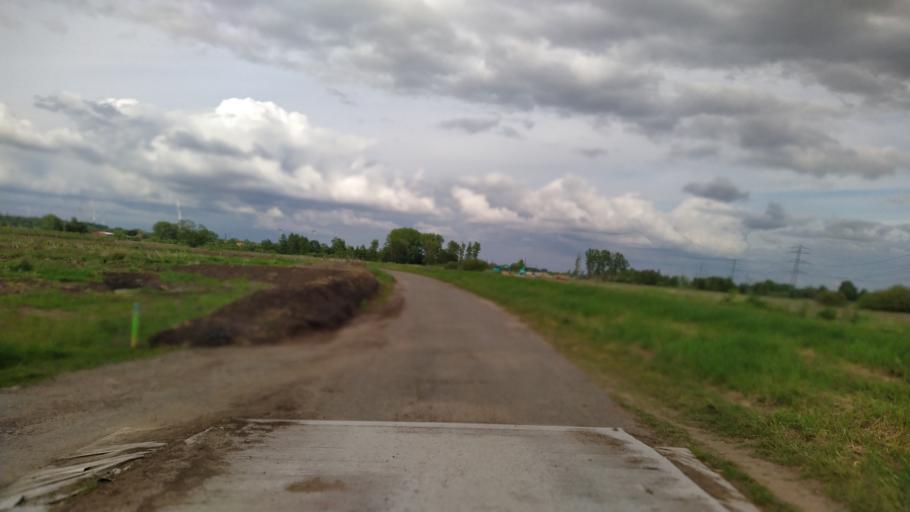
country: DE
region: Lower Saxony
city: Neu Wulmstorf
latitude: 53.4941
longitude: 9.8618
